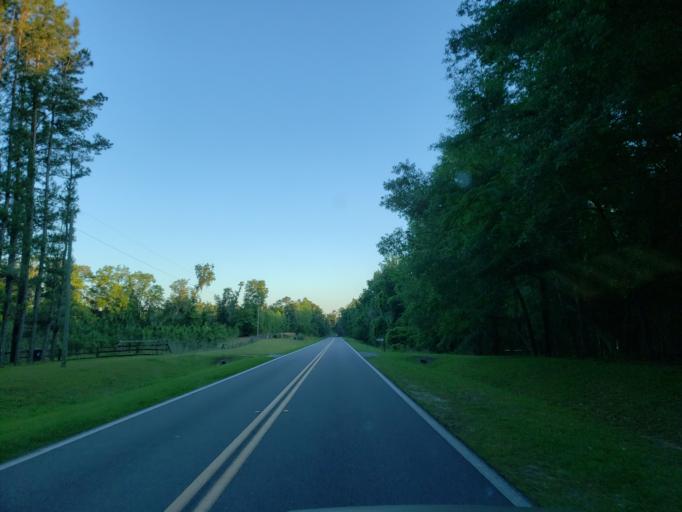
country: US
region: Florida
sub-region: Madison County
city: Madison
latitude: 30.6121
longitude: -83.2552
